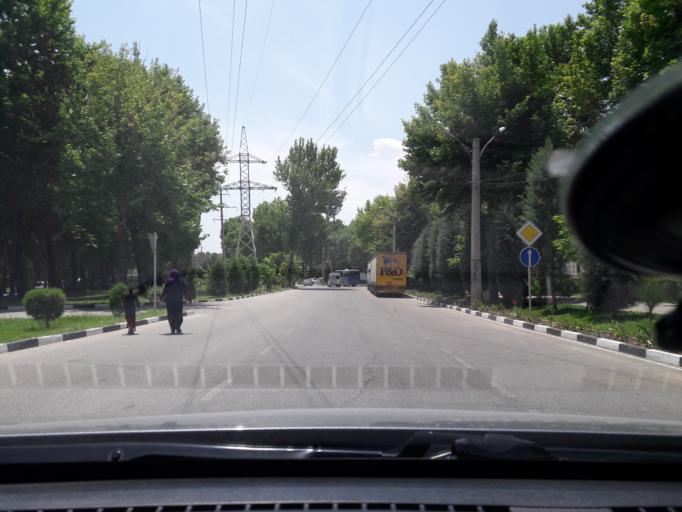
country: TJ
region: Dushanbe
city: Dushanbe
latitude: 38.5901
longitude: 68.7552
